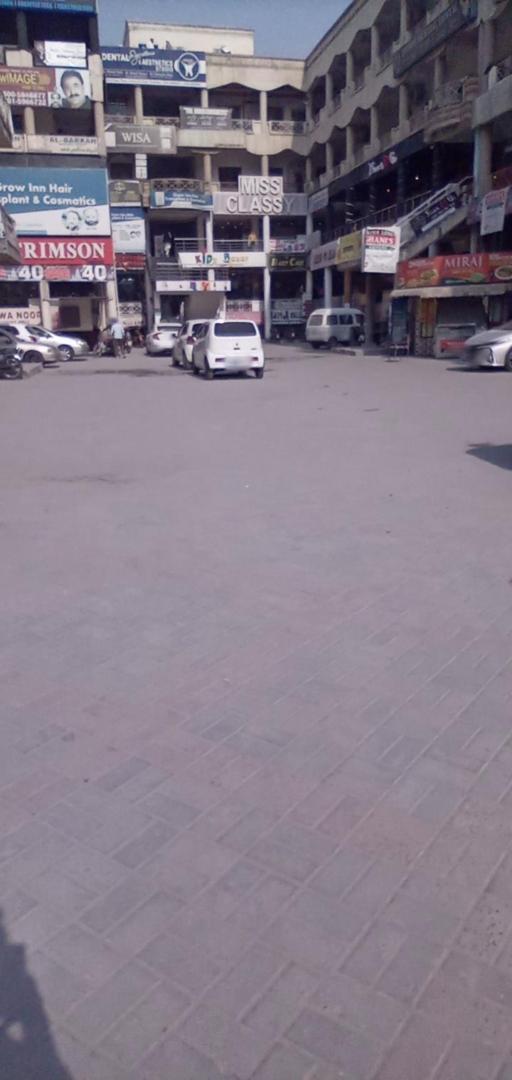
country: PK
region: Khyber Pakhtunkhwa
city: Peshawar
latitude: 34.0017
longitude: 71.4982
